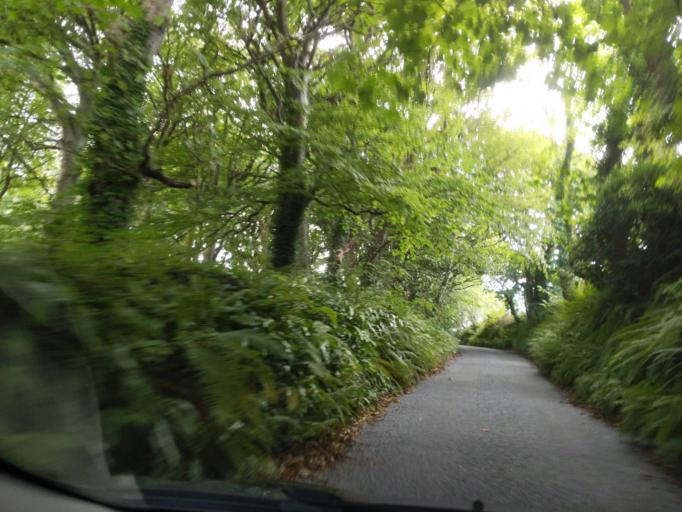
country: GB
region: England
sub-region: Plymouth
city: Plymstock
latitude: 50.3481
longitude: -4.1070
